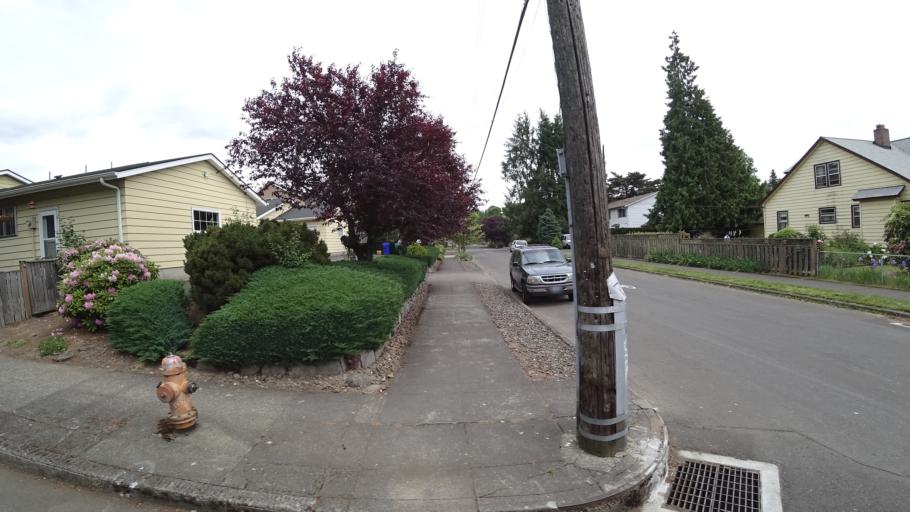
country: US
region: Oregon
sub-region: Multnomah County
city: Lents
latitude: 45.5250
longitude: -122.6064
